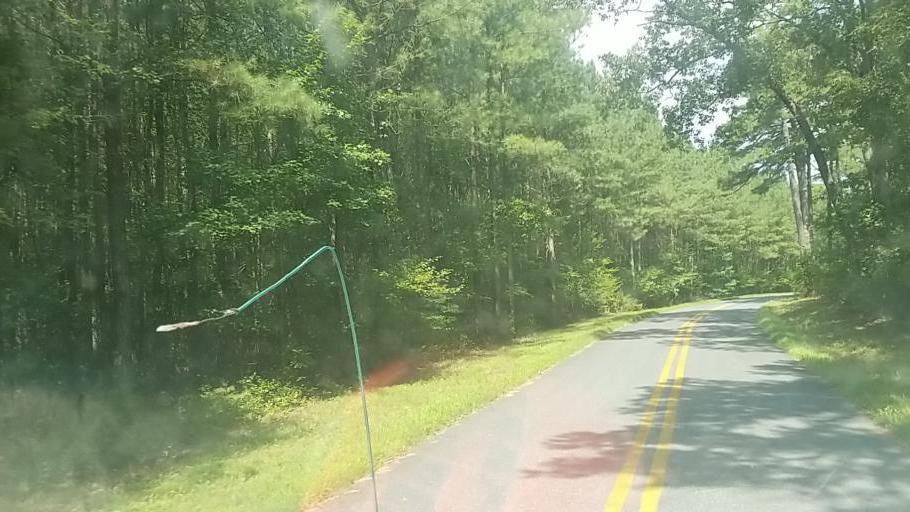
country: US
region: Maryland
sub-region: Wicomico County
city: Pittsville
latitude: 38.2810
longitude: -75.4750
